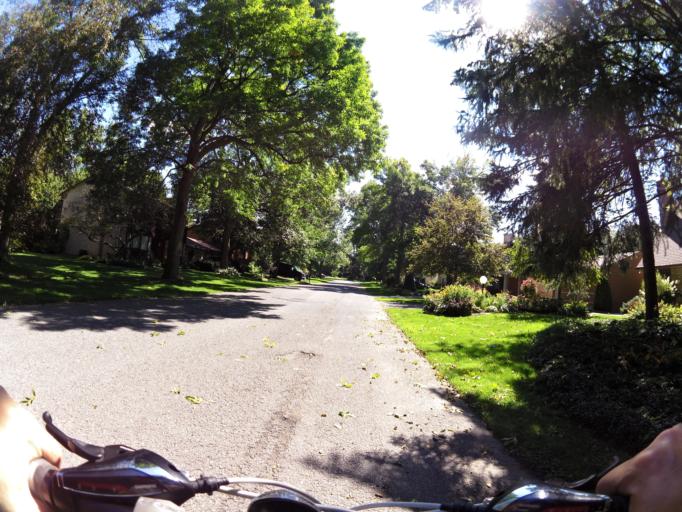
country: CA
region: Ontario
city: Bells Corners
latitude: 45.3258
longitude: -75.9083
